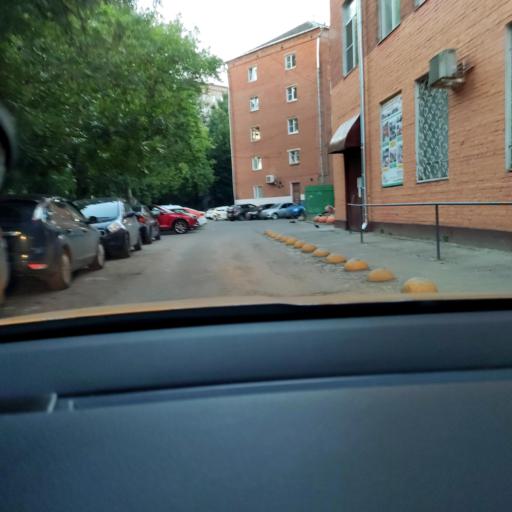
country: RU
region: Moskovskaya
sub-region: Podol'skiy Rayon
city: Podol'sk
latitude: 55.4293
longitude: 37.5215
